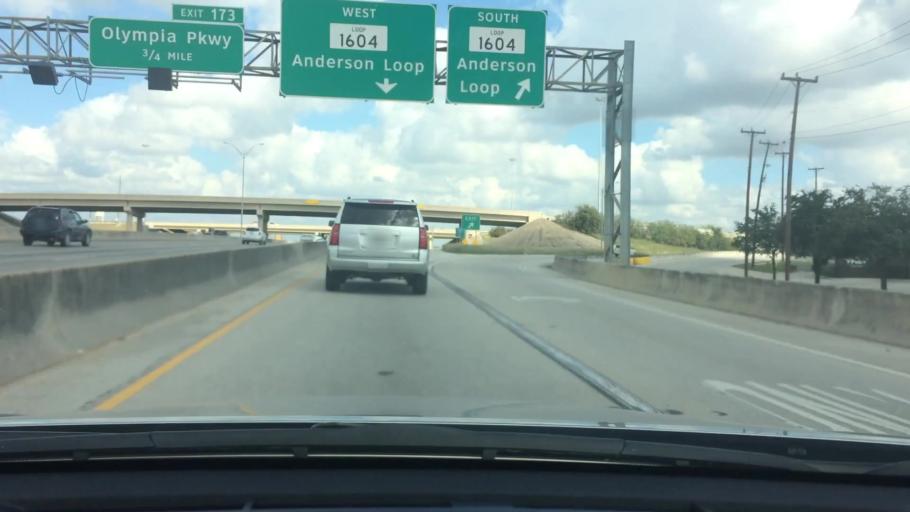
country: US
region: Texas
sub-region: Bexar County
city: Live Oak
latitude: 29.5658
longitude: -98.3354
